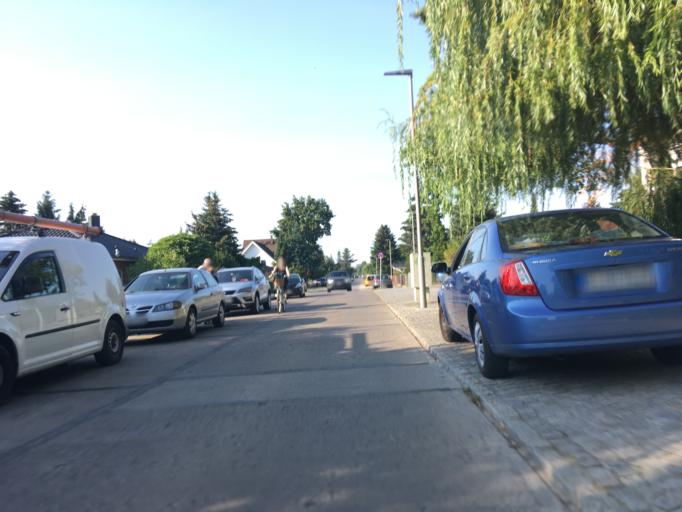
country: DE
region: Berlin
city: Berlin Koepenick
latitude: 52.4296
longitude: 13.5945
